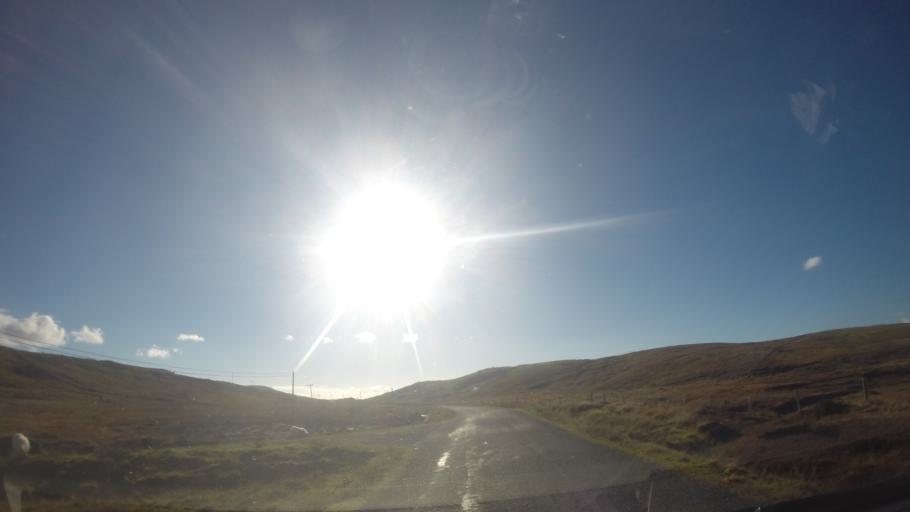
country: IE
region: Ulster
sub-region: County Donegal
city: Killybegs
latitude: 54.7033
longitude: -8.7679
